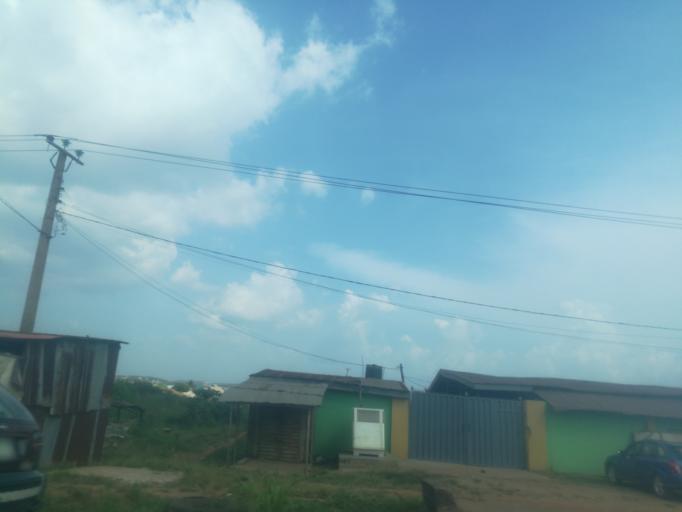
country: NG
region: Ogun
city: Abeokuta
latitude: 7.1201
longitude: 3.2981
